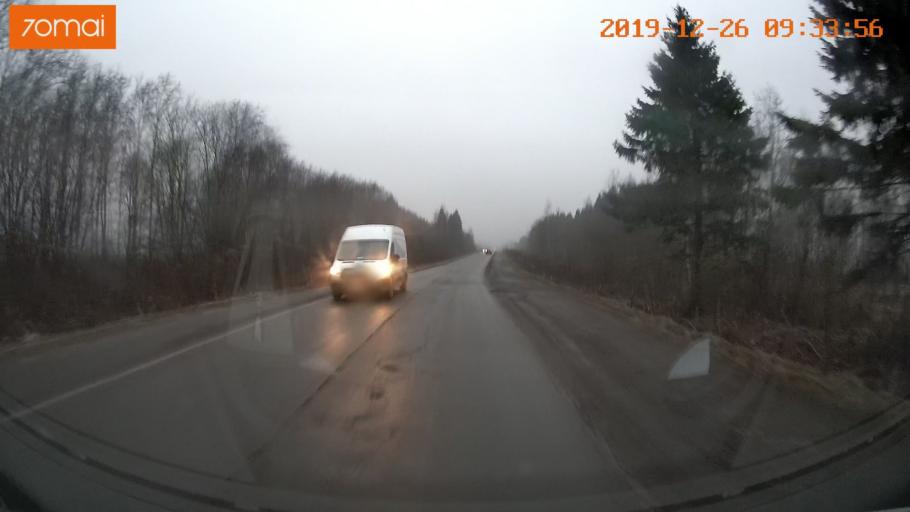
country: RU
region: Vologda
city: Vologda
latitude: 59.0956
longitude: 40.0930
